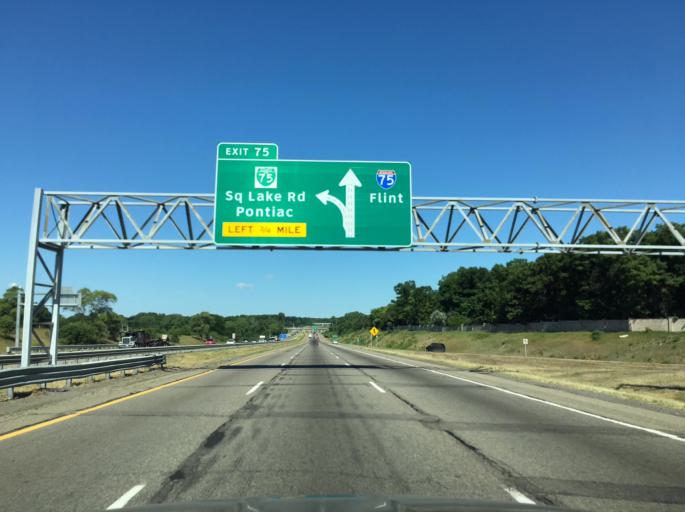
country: US
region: Michigan
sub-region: Oakland County
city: Bloomfield Hills
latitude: 42.6078
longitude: -83.2127
